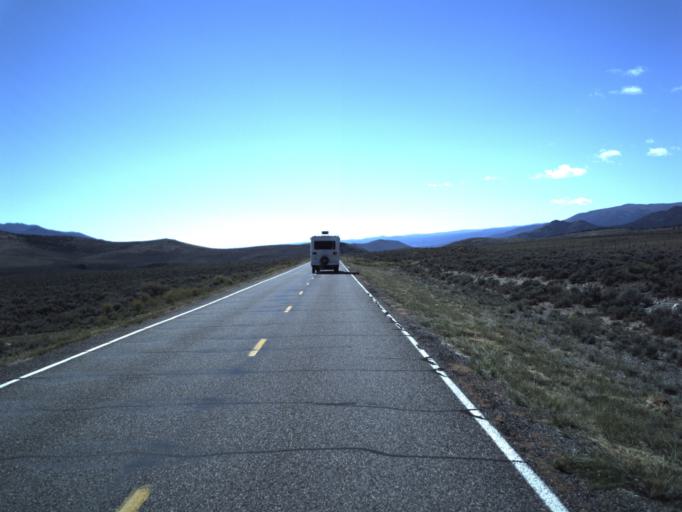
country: US
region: Utah
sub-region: Wayne County
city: Loa
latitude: 38.3780
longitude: -111.9367
